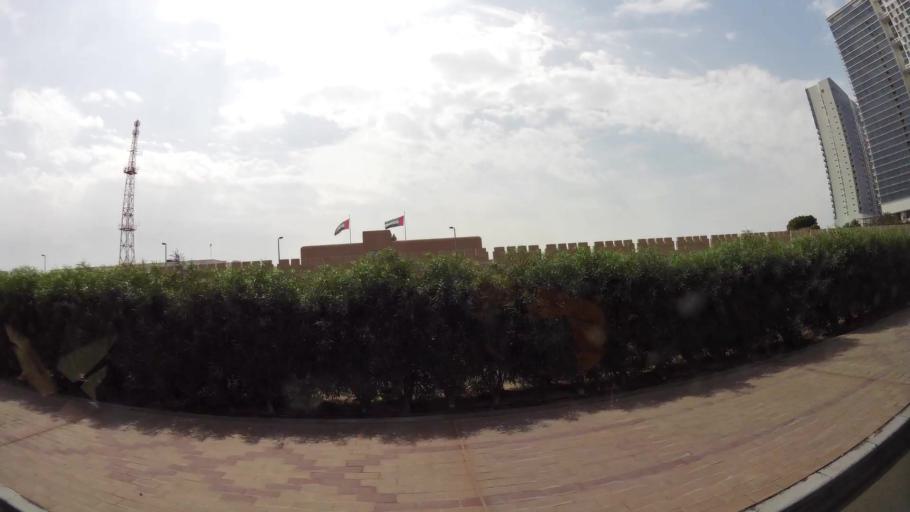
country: AE
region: Abu Dhabi
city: Abu Dhabi
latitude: 24.4139
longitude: 54.4659
